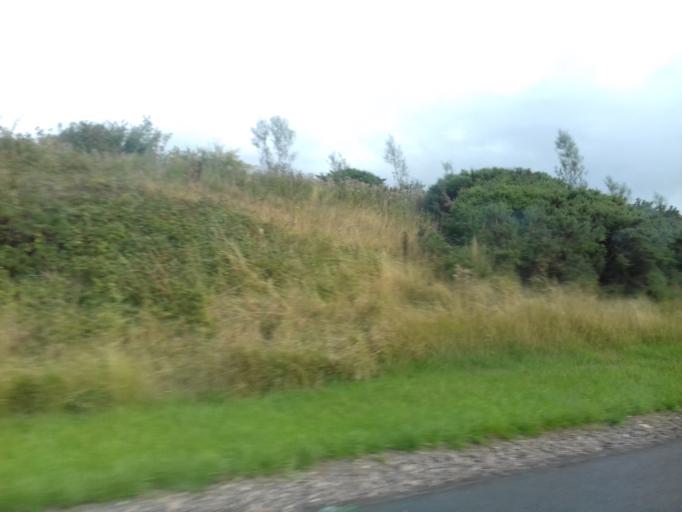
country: IE
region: Leinster
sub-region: Kilkenny
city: Mooncoin
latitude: 52.3467
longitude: -7.1664
